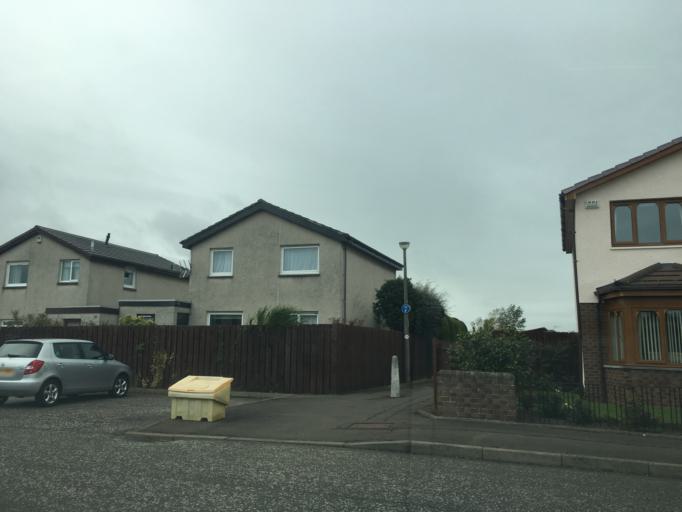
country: GB
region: Scotland
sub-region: Edinburgh
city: Colinton
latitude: 55.9014
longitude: -3.2193
